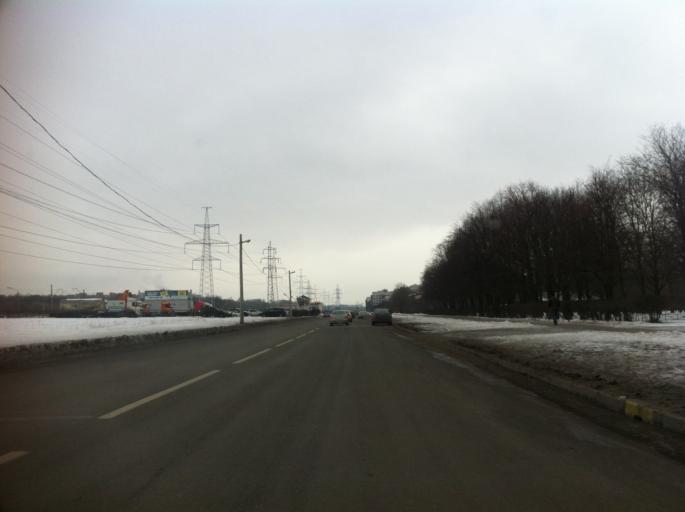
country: RU
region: St.-Petersburg
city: Uritsk
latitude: 59.8474
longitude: 30.1702
